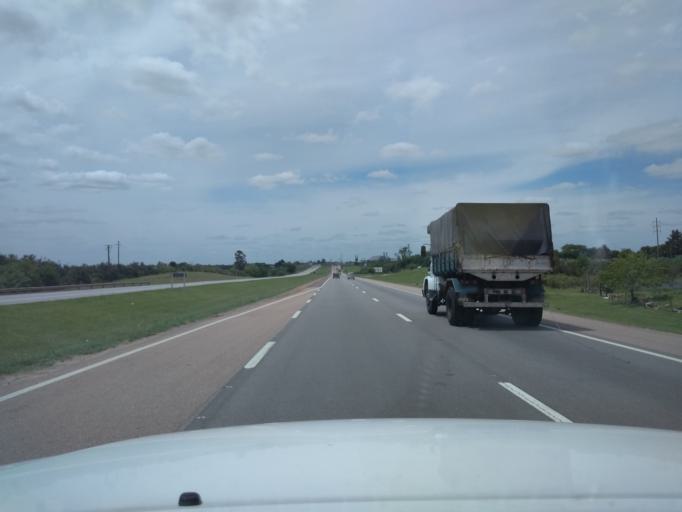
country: UY
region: Canelones
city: La Paz
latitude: -34.7581
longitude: -56.2602
